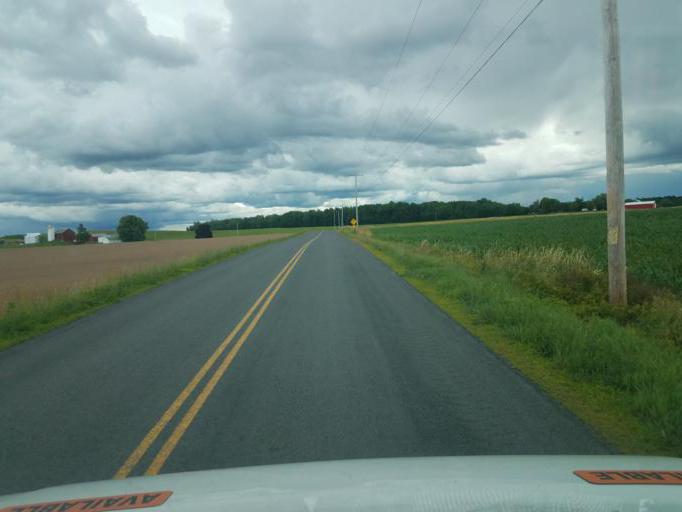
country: US
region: New York
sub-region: Seneca County
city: Waterloo
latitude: 42.9735
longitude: -76.9374
